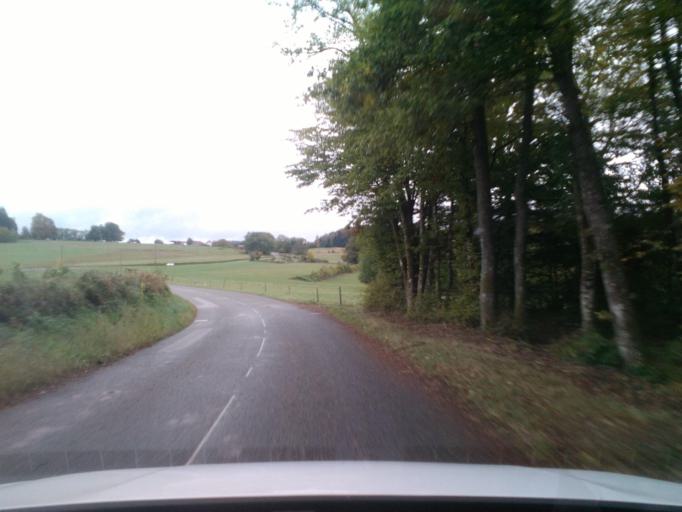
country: FR
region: Lorraine
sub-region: Departement des Vosges
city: Senones
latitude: 48.3661
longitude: 6.9649
